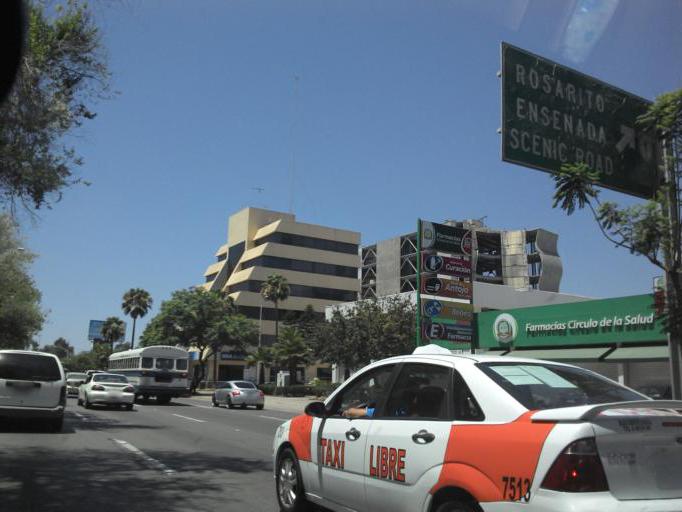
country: MX
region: Baja California
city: Tijuana
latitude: 32.5303
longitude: -117.0251
